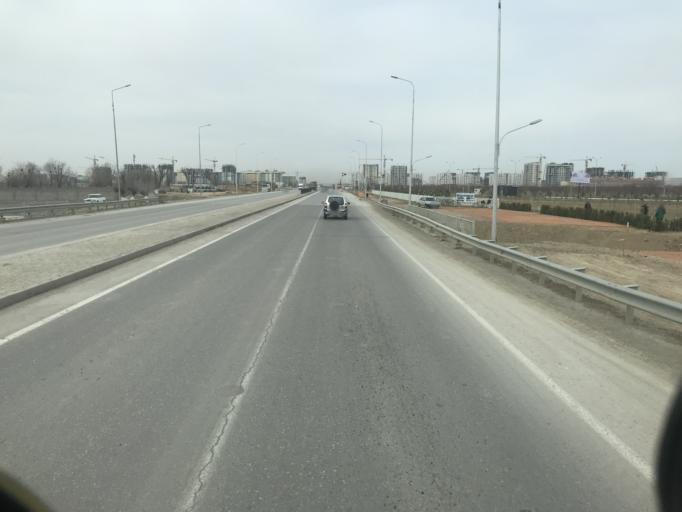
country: KZ
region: Ongtustik Qazaqstan
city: Turkestan
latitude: 43.2668
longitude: 68.3602
